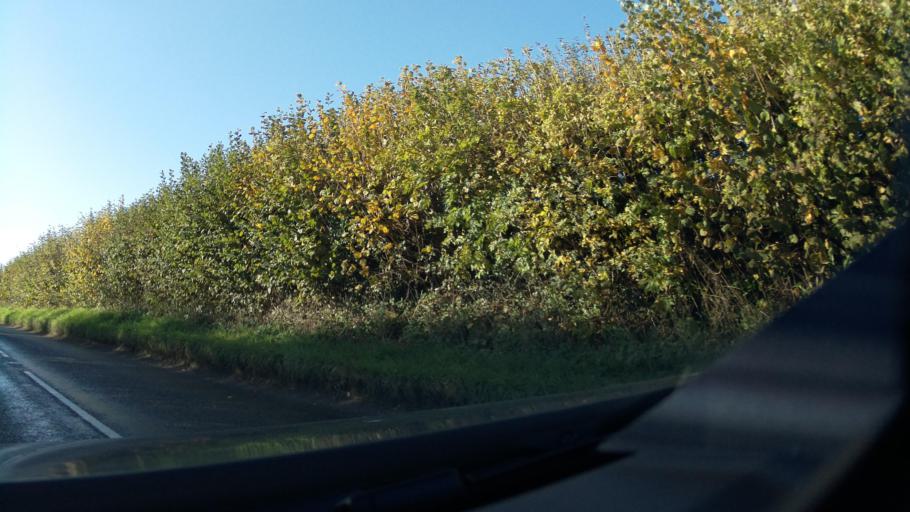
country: GB
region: England
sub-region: Somerset
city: Bruton
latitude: 51.1256
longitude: -2.4374
